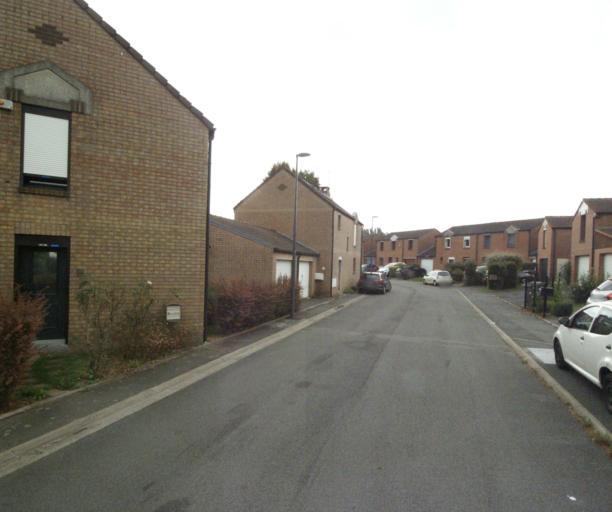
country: FR
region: Nord-Pas-de-Calais
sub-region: Departement du Nord
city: Mons-en-Baroeul
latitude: 50.6423
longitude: 3.1360
